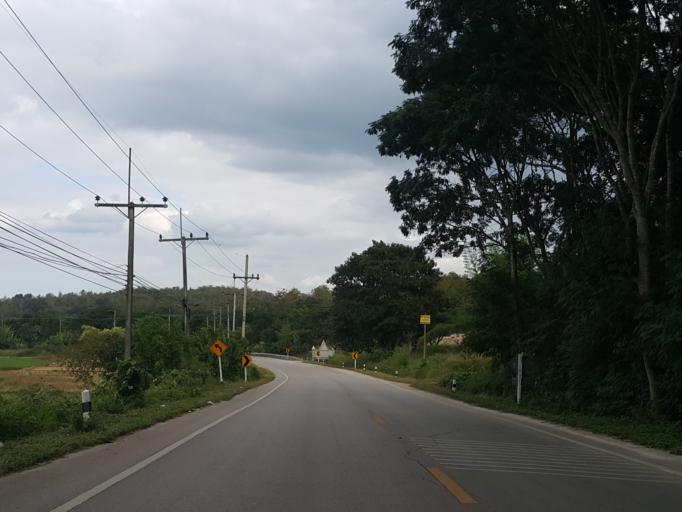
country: TH
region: Lampang
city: Chae Hom
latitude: 18.5776
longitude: 99.4701
